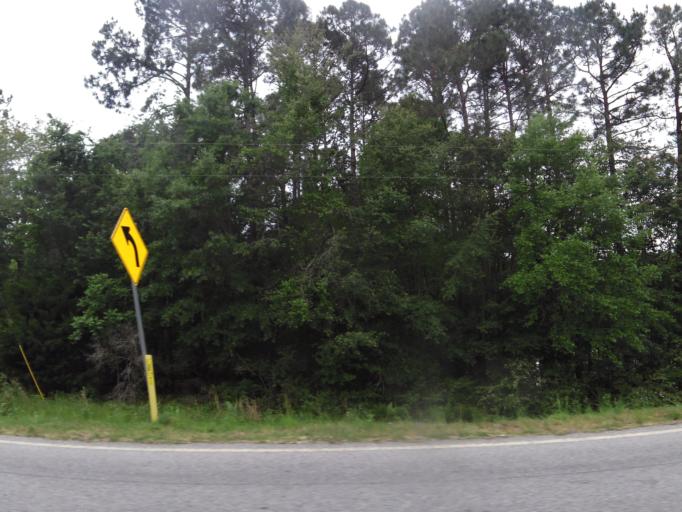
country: US
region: Georgia
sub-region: Emanuel County
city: Twin City
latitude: 32.4499
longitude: -82.2207
